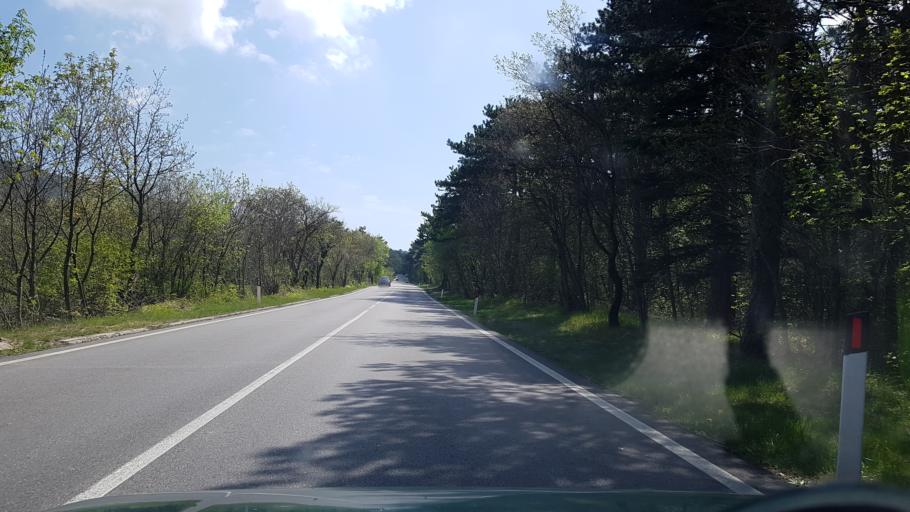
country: IT
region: Friuli Venezia Giulia
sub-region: Provincia di Trieste
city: Dolina
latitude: 45.6364
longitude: 13.8742
